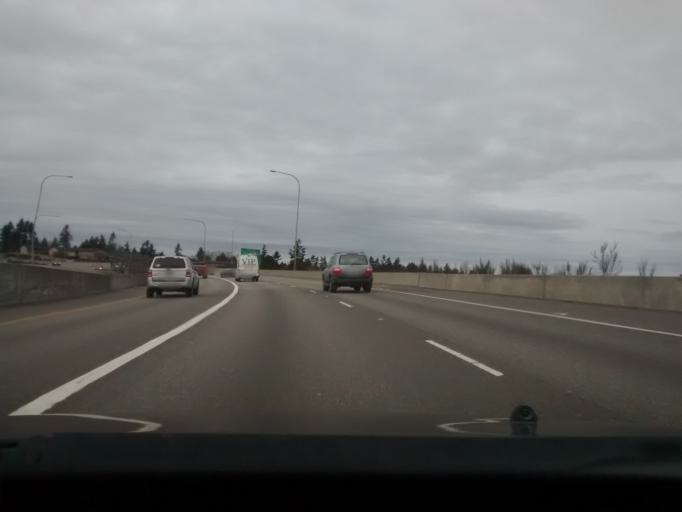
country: US
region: Washington
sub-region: Pierce County
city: Fircrest
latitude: 47.2568
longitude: -122.5149
